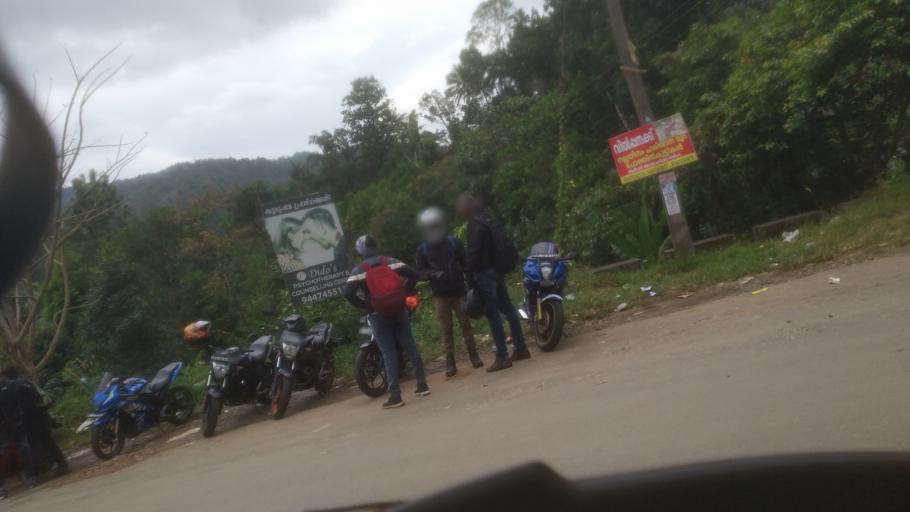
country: IN
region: Kerala
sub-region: Idukki
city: Idukki
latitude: 9.9744
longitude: 76.9973
